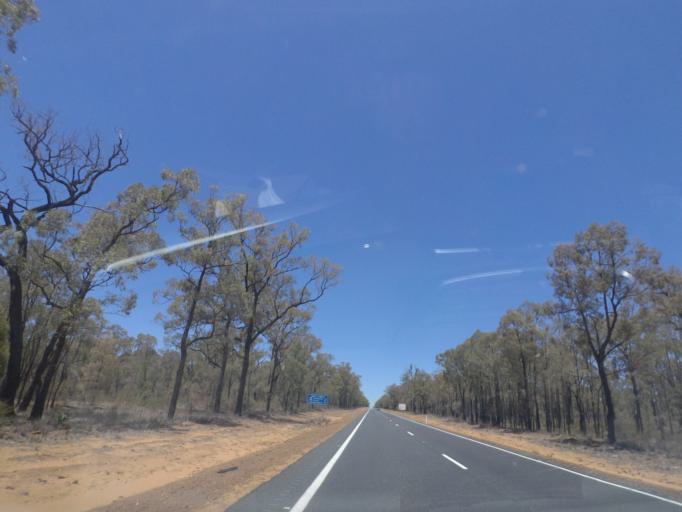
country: AU
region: New South Wales
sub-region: Narrabri
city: Narrabri
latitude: -30.7259
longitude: 149.5230
